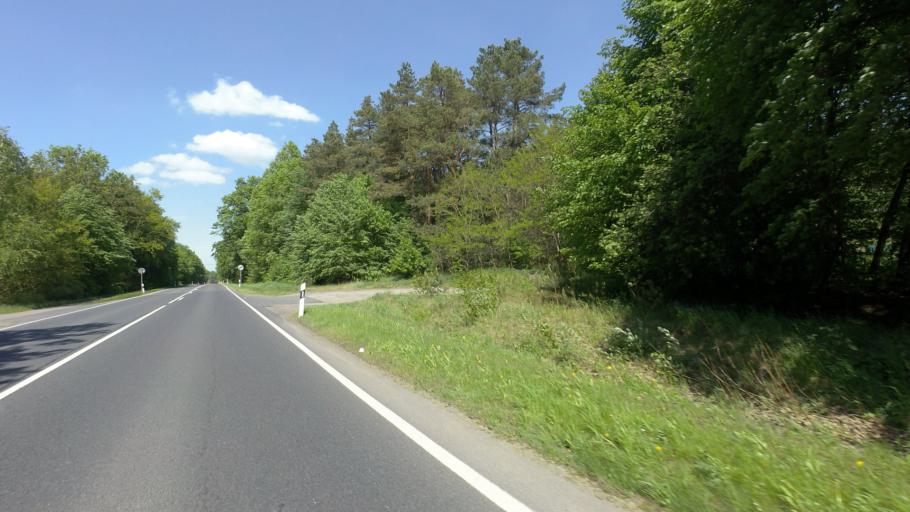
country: DE
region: Mecklenburg-Vorpommern
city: Neustrelitz
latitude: 53.3880
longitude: 13.0471
